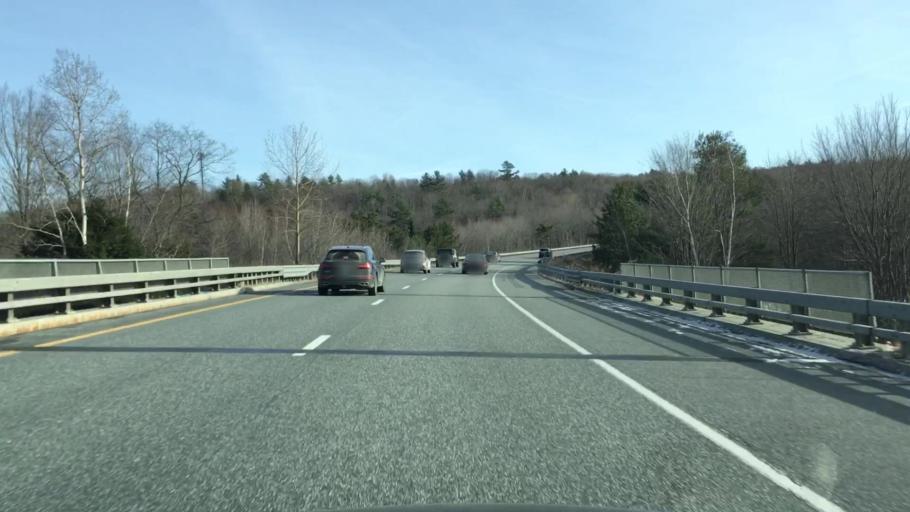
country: US
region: New Hampshire
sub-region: Sullivan County
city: Grantham
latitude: 43.4898
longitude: -72.1108
